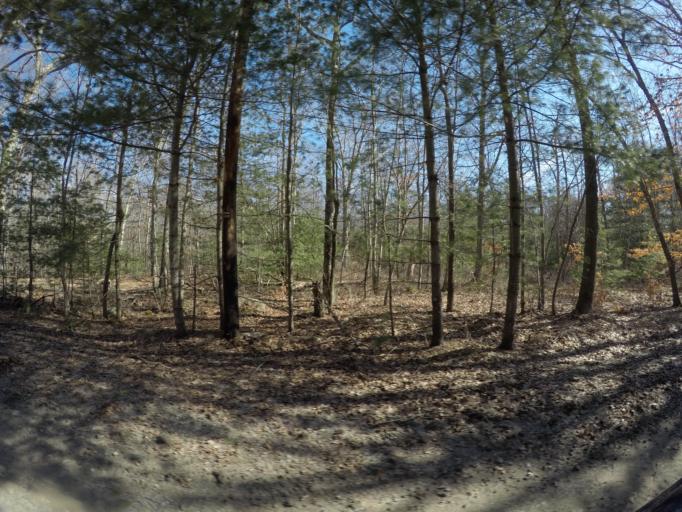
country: US
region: Massachusetts
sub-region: Norfolk County
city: Sharon
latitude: 42.0875
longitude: -71.1498
